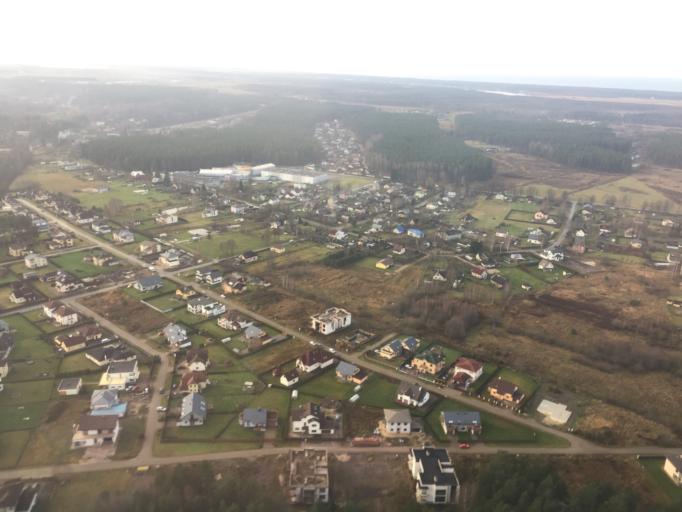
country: LV
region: Babite
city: Pinki
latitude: 56.9622
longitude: 23.9786
